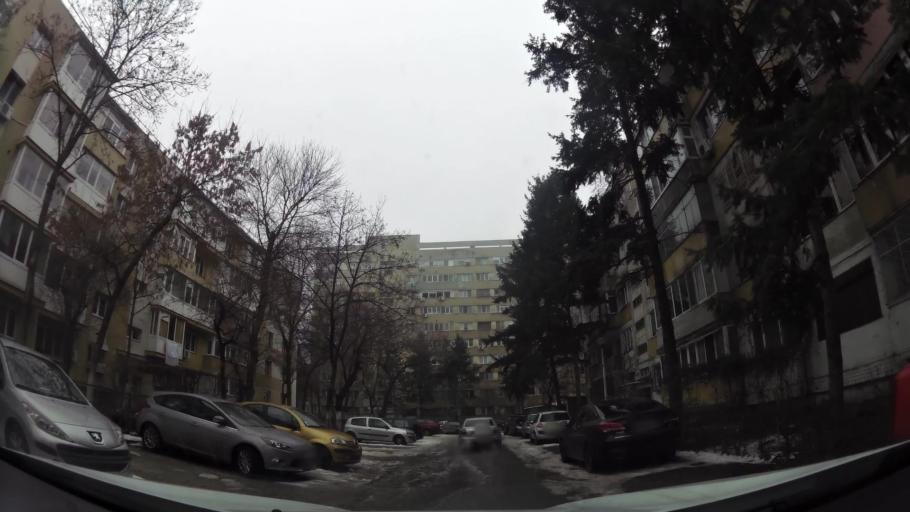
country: RO
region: Ilfov
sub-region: Comuna Chiajna
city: Rosu
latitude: 44.4373
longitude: 26.0195
